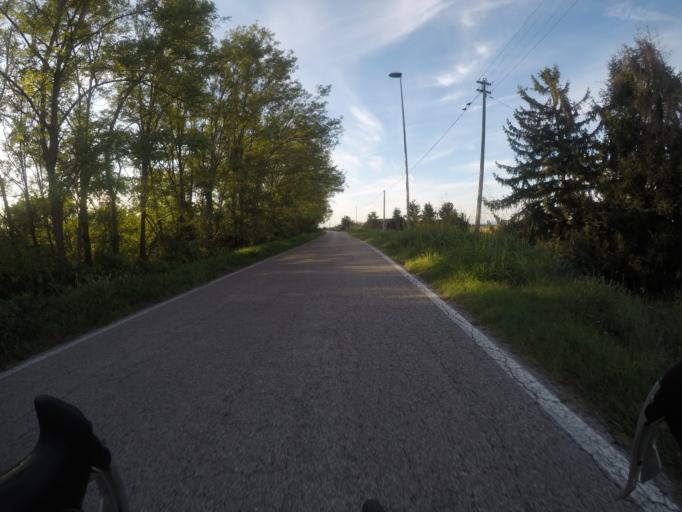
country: IT
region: Veneto
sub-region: Provincia di Rovigo
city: San Bellino
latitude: 45.0152
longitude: 11.5657
